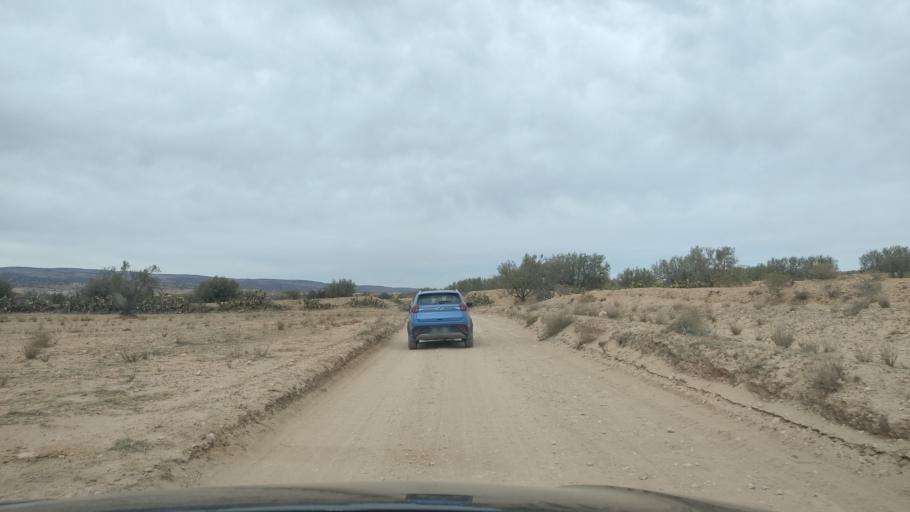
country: TN
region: Al Qasrayn
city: Kasserine
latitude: 35.2524
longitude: 8.9218
